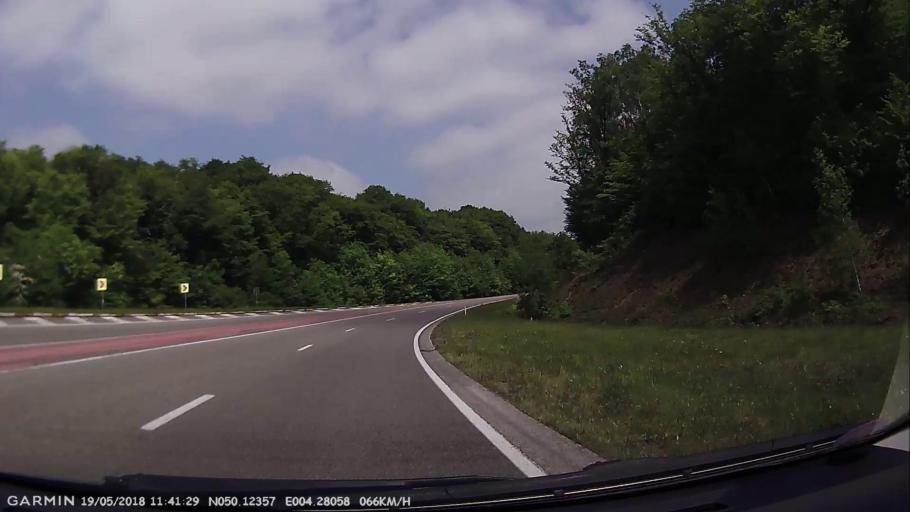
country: BE
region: Wallonia
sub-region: Province du Hainaut
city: Froidchapelle
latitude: 50.1238
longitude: 4.2804
